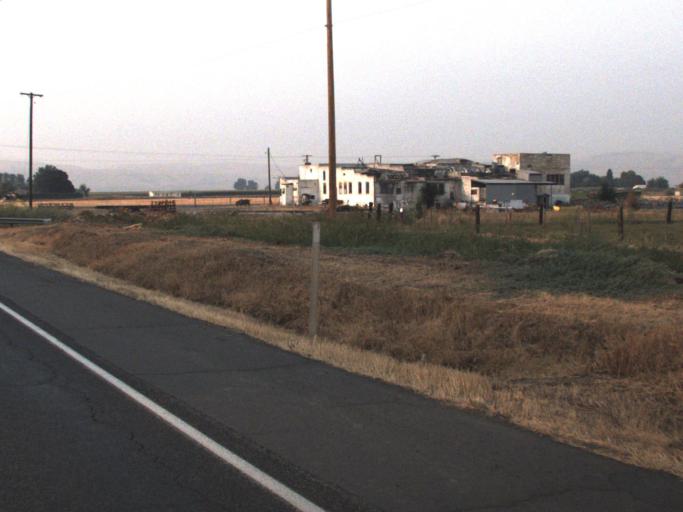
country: US
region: Washington
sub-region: Yakima County
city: Toppenish
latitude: 46.3623
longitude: -120.3202
